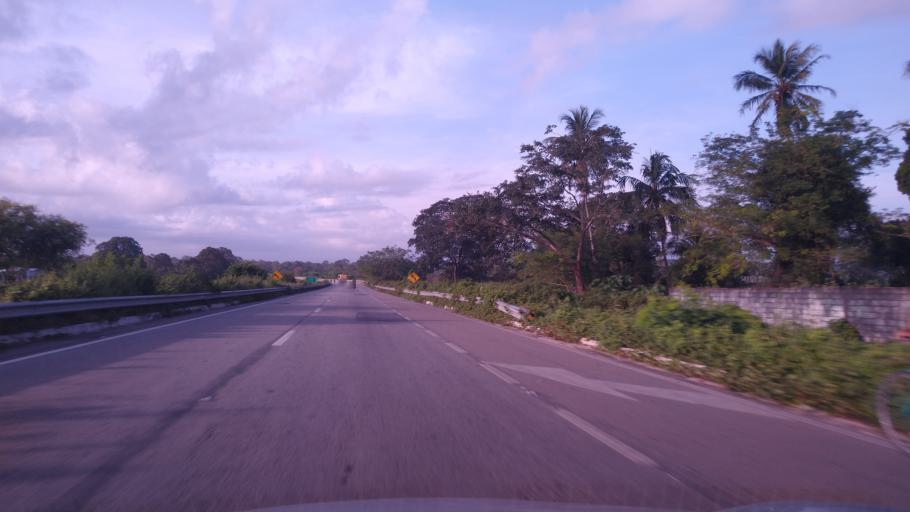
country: BR
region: Ceara
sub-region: Pacajus
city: Pacajus
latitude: -4.1778
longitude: -38.4923
